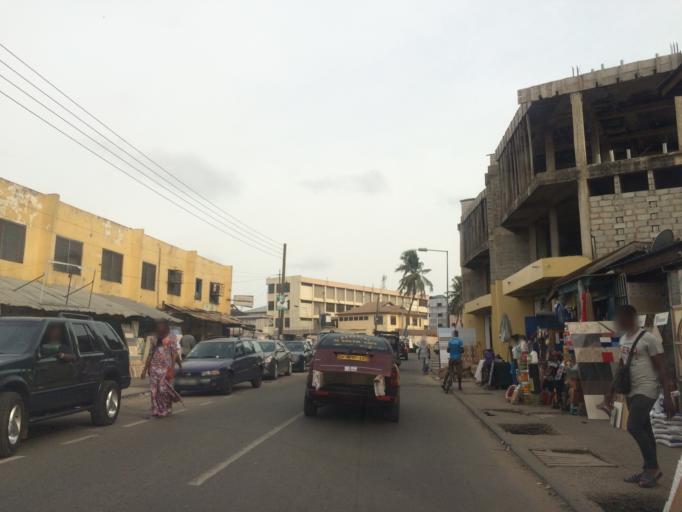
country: GH
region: Greater Accra
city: Accra
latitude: 5.5455
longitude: -0.2143
